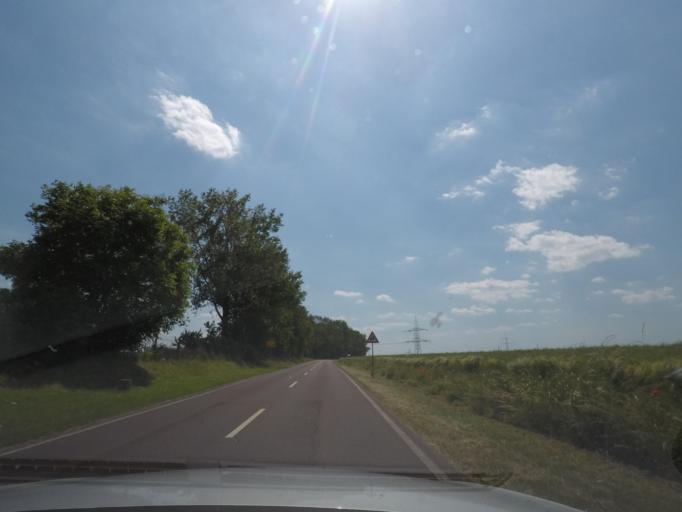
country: DE
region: Saxony-Anhalt
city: Haldensleben I
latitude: 52.2427
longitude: 11.3968
